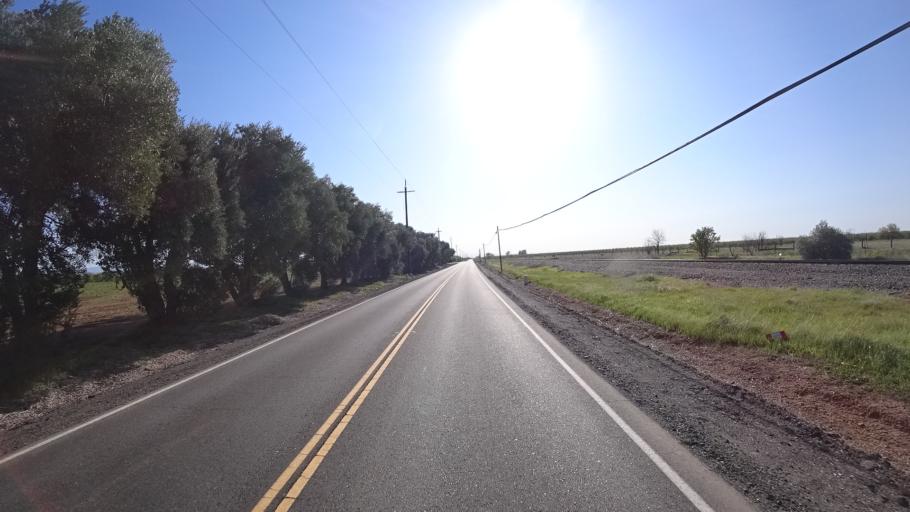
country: US
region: California
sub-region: Glenn County
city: Orland
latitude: 39.7684
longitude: -122.1067
